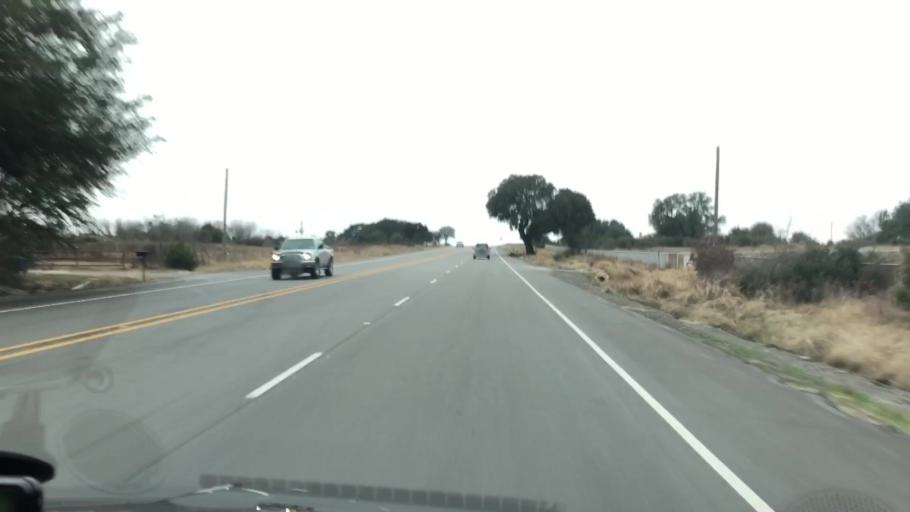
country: US
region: Texas
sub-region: Hamilton County
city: Hico
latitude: 32.0014
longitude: -98.0520
